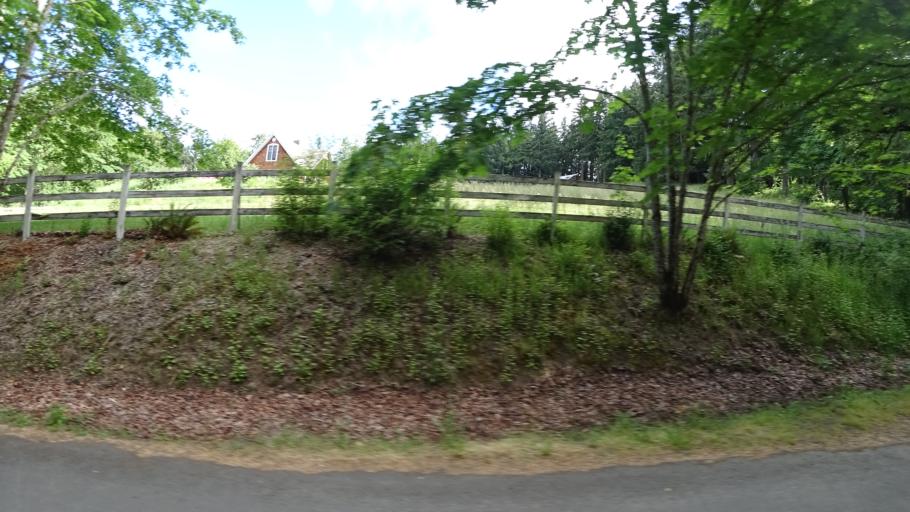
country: US
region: Oregon
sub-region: Washington County
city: Oak Hills
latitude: 45.5787
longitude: -122.8137
